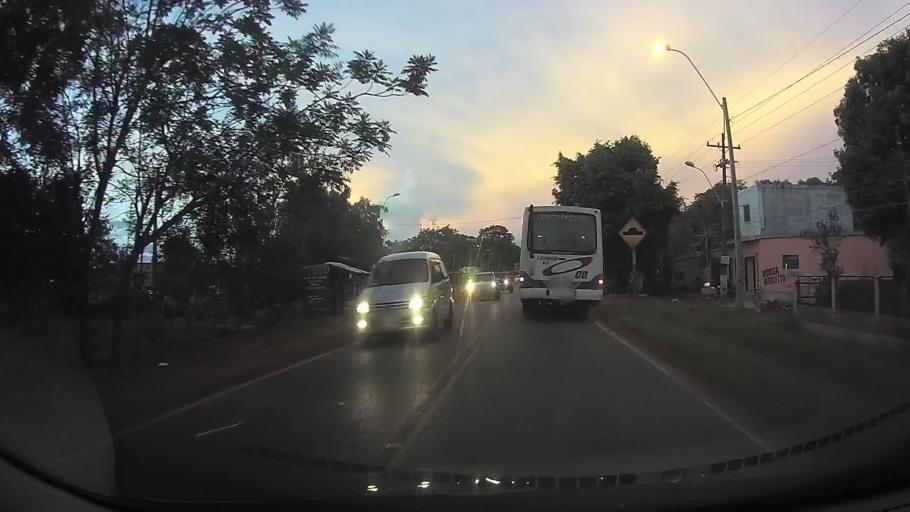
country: PY
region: Central
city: Ita
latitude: -25.4808
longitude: -57.3618
